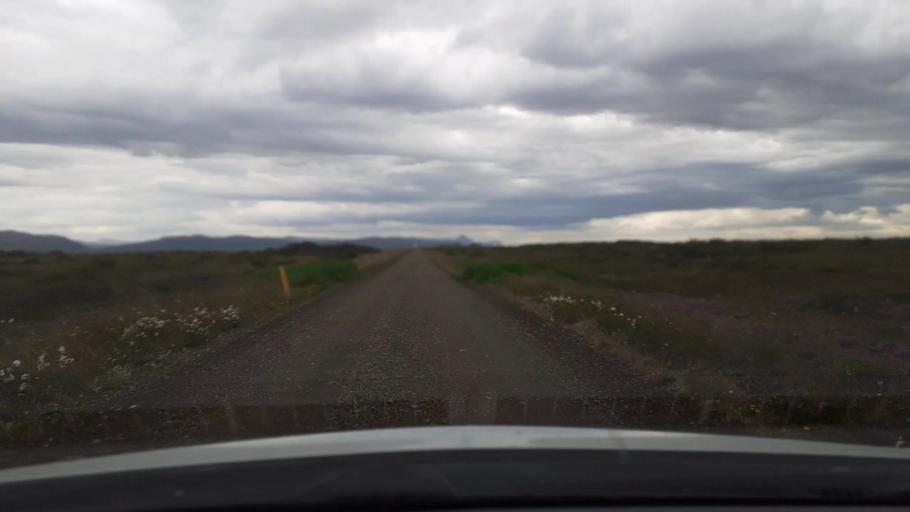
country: IS
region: West
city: Borgarnes
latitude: 64.6412
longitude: -21.9015
